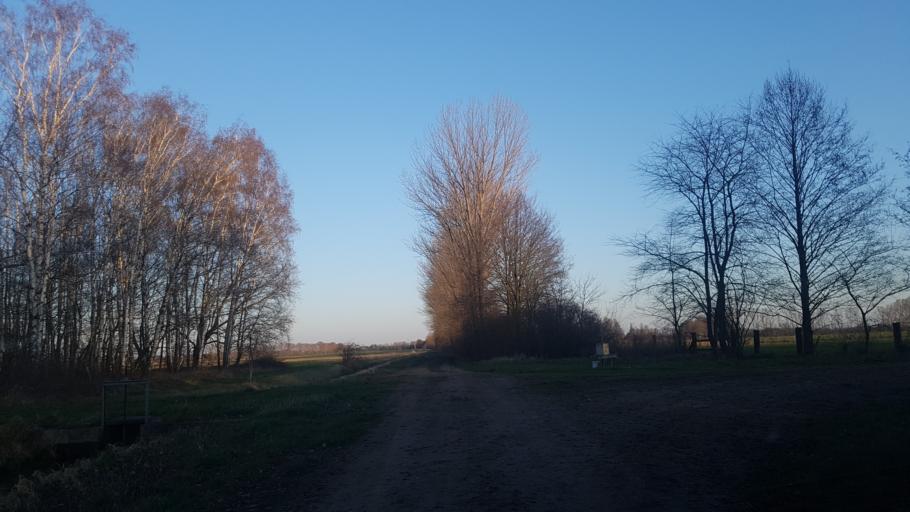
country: DE
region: Brandenburg
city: Bad Liebenwerda
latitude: 51.5284
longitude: 13.3559
